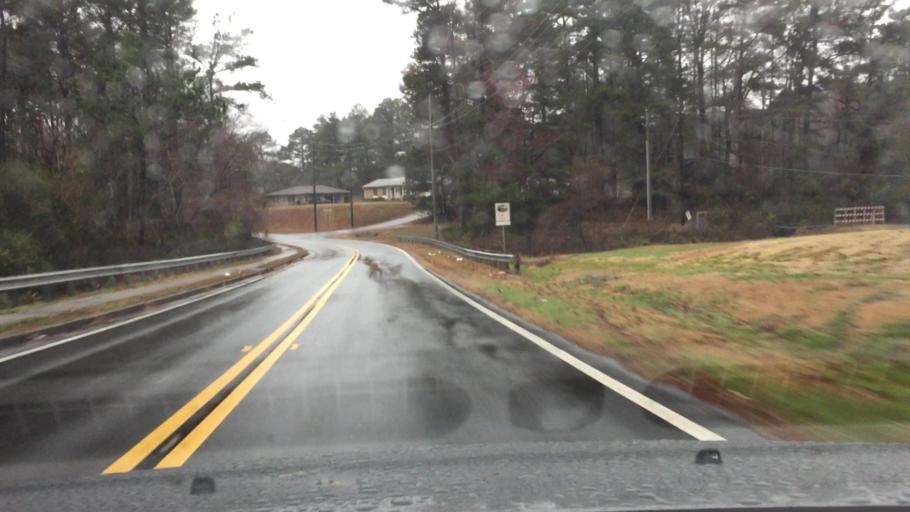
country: US
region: Georgia
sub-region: Cobb County
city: Fair Oaks
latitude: 33.9088
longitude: -84.5688
